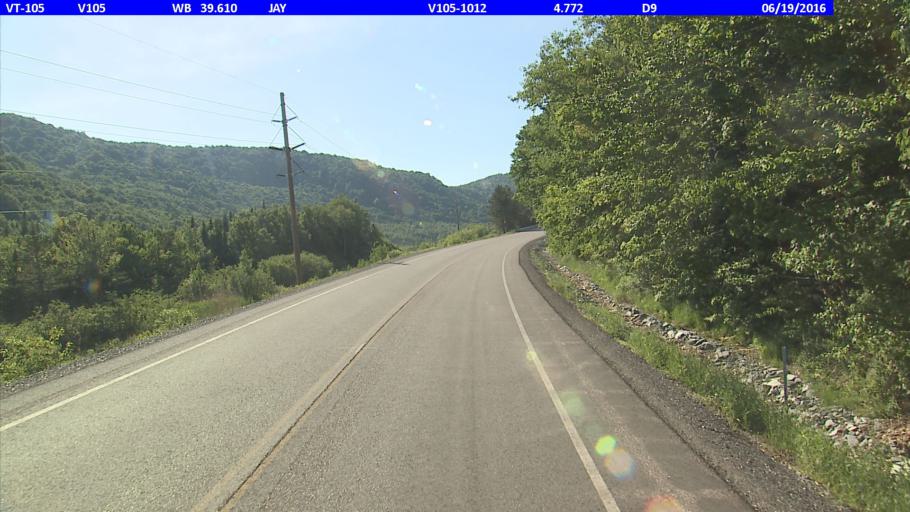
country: CA
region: Quebec
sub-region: Monteregie
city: Sutton
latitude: 44.9818
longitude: -72.4889
